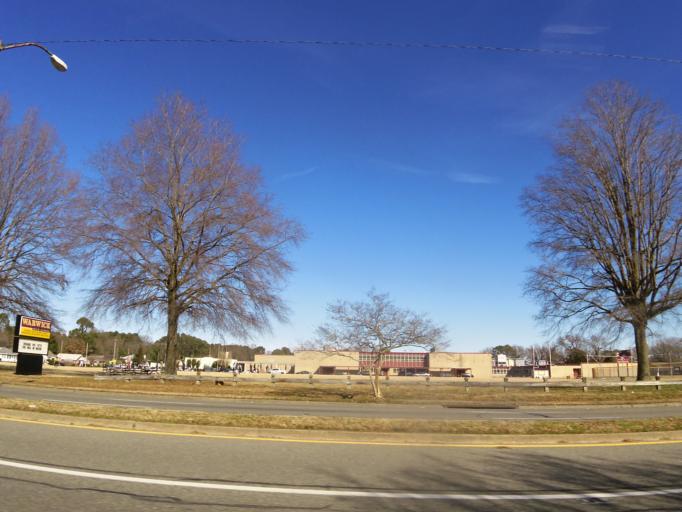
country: US
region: Virginia
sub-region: City of Newport News
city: Newport News
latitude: 37.0515
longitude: -76.4777
